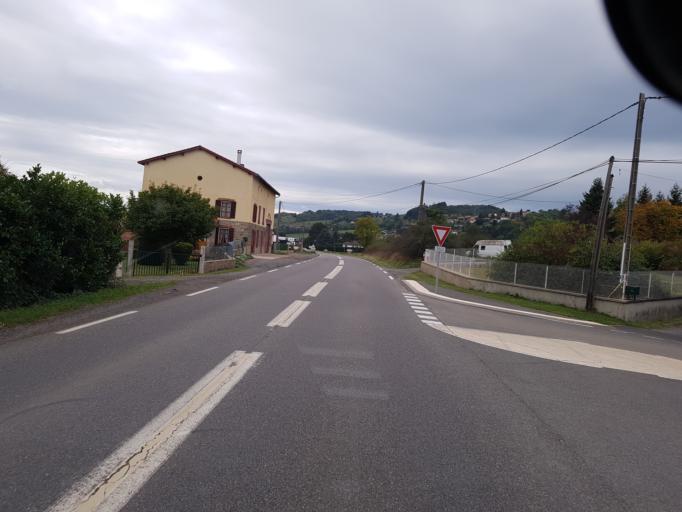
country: FR
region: Rhone-Alpes
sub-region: Departement du Rhone
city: Sainte-Foy-l'Argentiere
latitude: 45.7141
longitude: 4.4806
